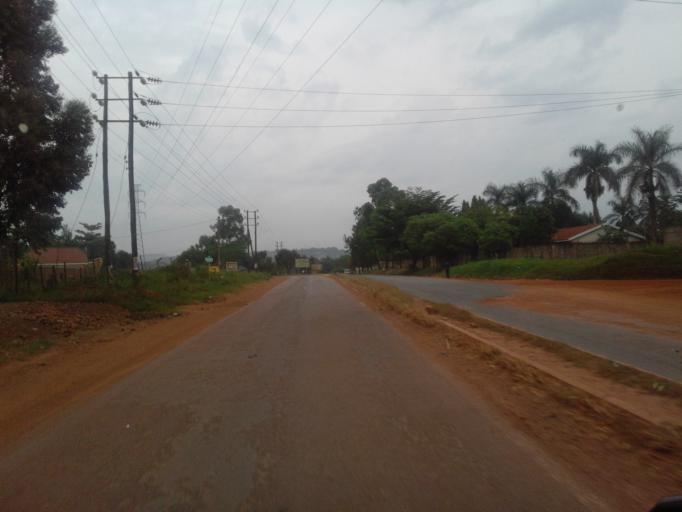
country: UG
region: Central Region
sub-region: Buikwe District
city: Njeru
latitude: 0.4390
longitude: 33.1759
